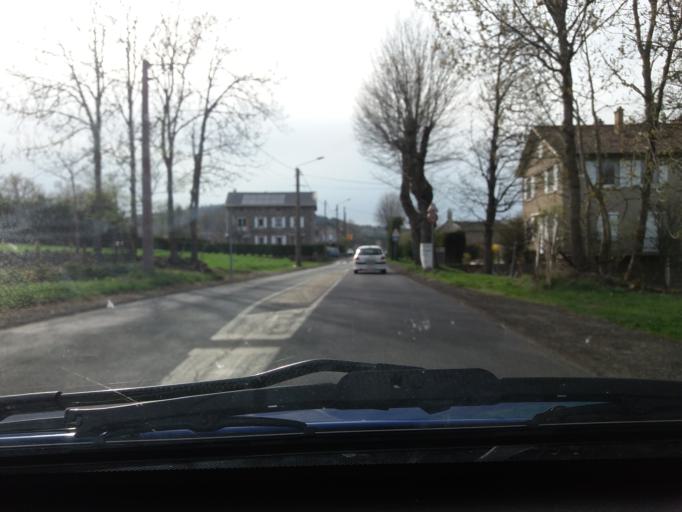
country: FR
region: Auvergne
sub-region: Departement de la Haute-Loire
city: Mazet-Saint-Voy
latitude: 45.0769
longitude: 4.2185
